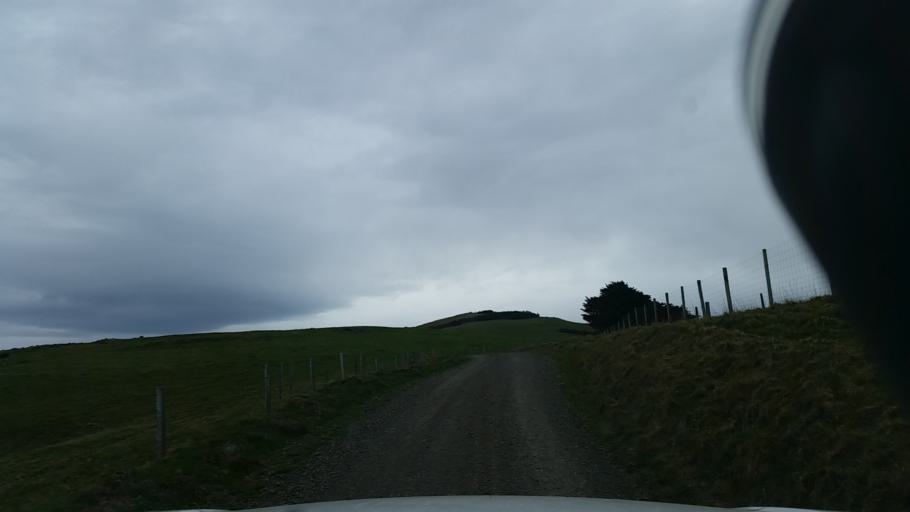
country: NZ
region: Canterbury
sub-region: Christchurch City
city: Christchurch
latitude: -43.8213
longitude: 173.0735
